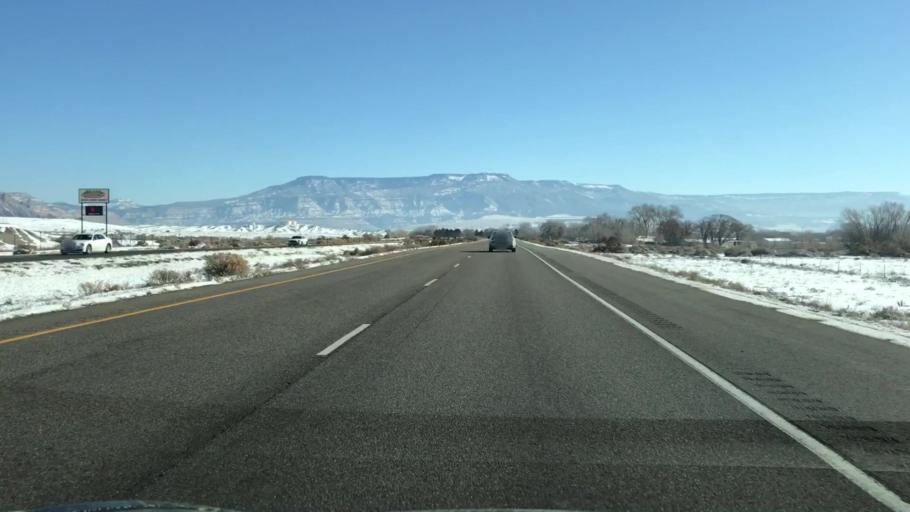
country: US
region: Colorado
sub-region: Mesa County
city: Fruitvale
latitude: 39.1067
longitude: -108.4928
